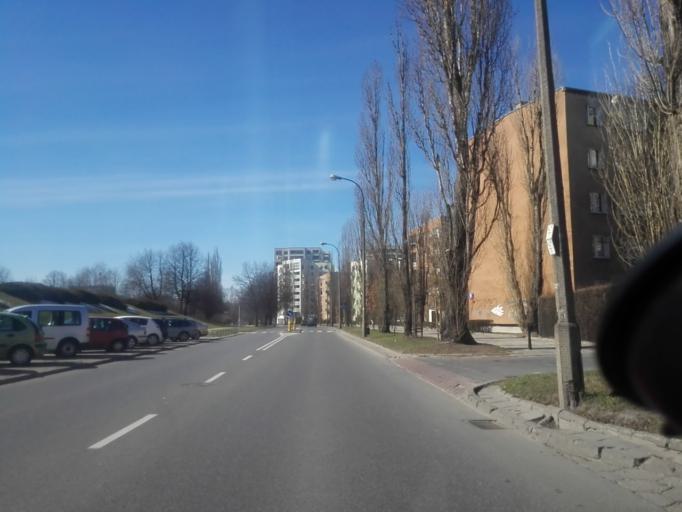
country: PL
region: Masovian Voivodeship
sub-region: Warszawa
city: Ochota
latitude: 52.2005
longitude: 20.9781
